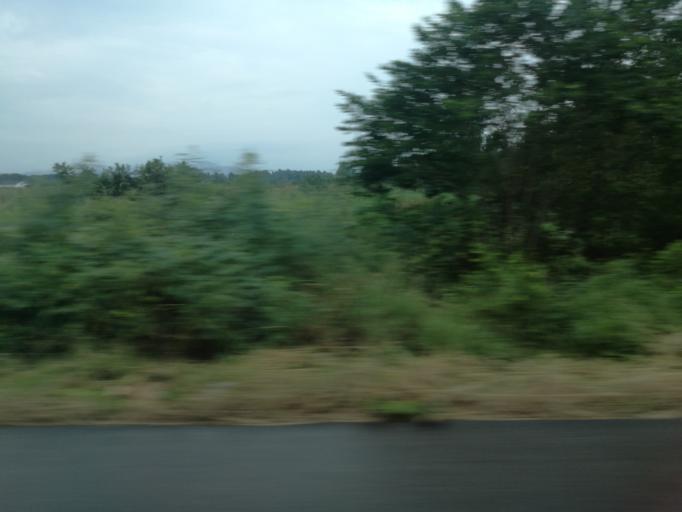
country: TH
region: Prachuap Khiri Khan
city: Kui Buri
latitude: 12.0977
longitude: 99.8536
